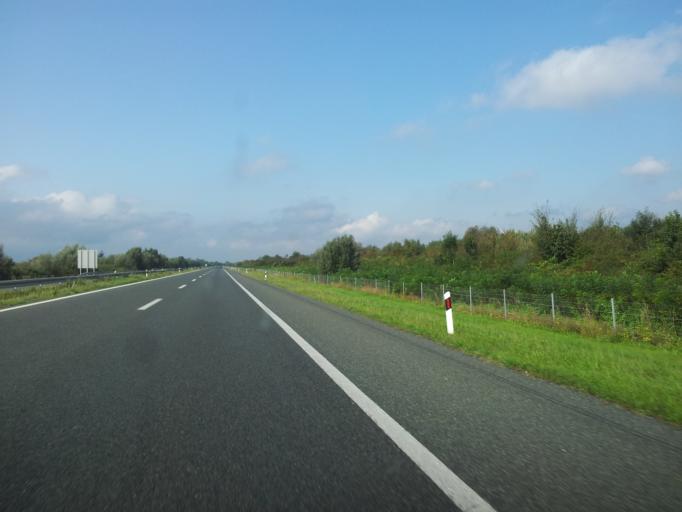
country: HR
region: Brodsko-Posavska
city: Oriovac
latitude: 45.1539
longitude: 17.7998
